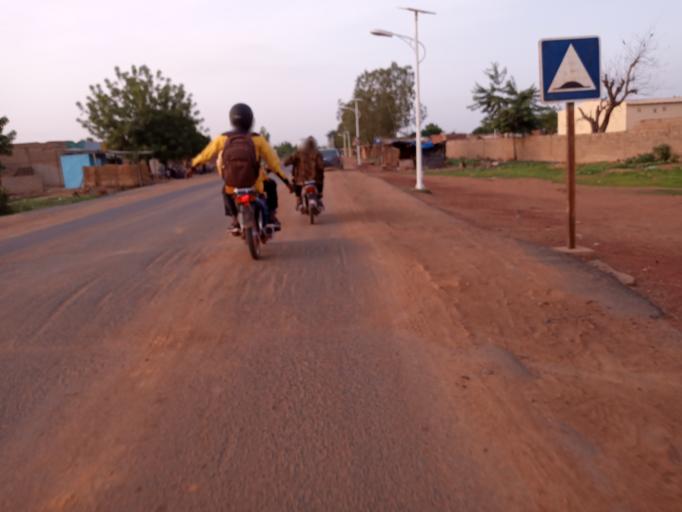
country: ML
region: Bamako
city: Bamako
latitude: 12.3079
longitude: -8.1544
